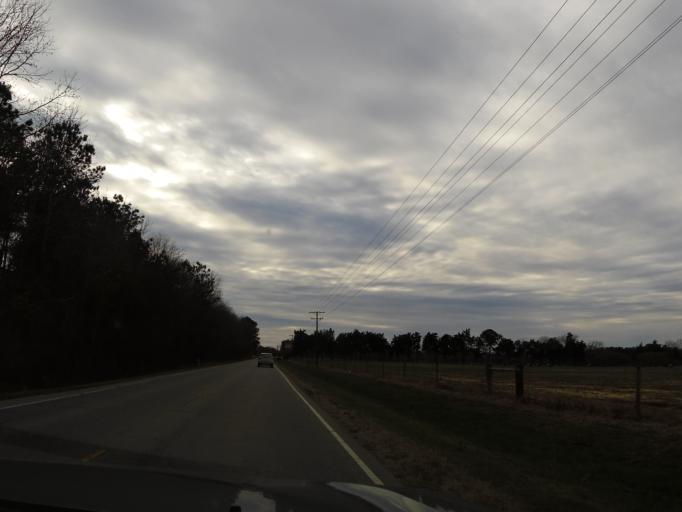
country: US
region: North Carolina
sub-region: Nash County
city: Rocky Mount
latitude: 35.9773
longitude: -77.7281
